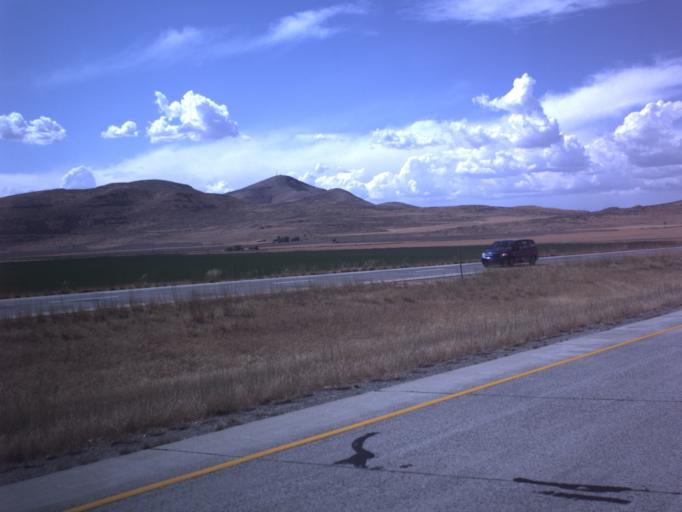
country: US
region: Utah
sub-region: Box Elder County
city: Garland
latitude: 41.7637
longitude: -112.2639
